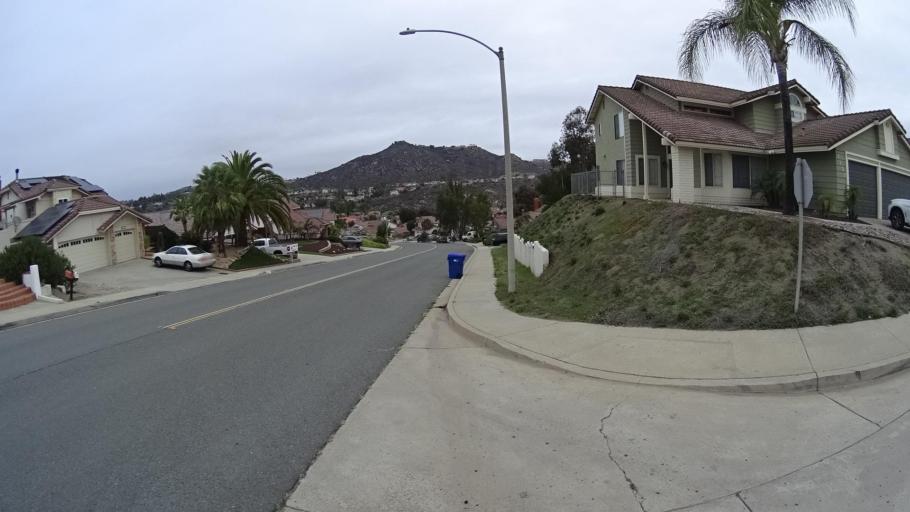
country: US
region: California
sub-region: San Diego County
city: Rancho San Diego
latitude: 32.7557
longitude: -116.9091
